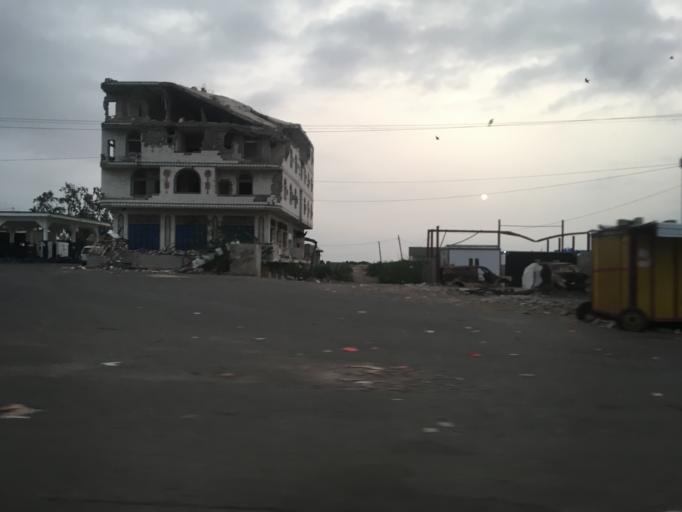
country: YE
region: Lahij
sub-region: Al  Hawtah
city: Lahij
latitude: 13.0228
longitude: 44.8920
